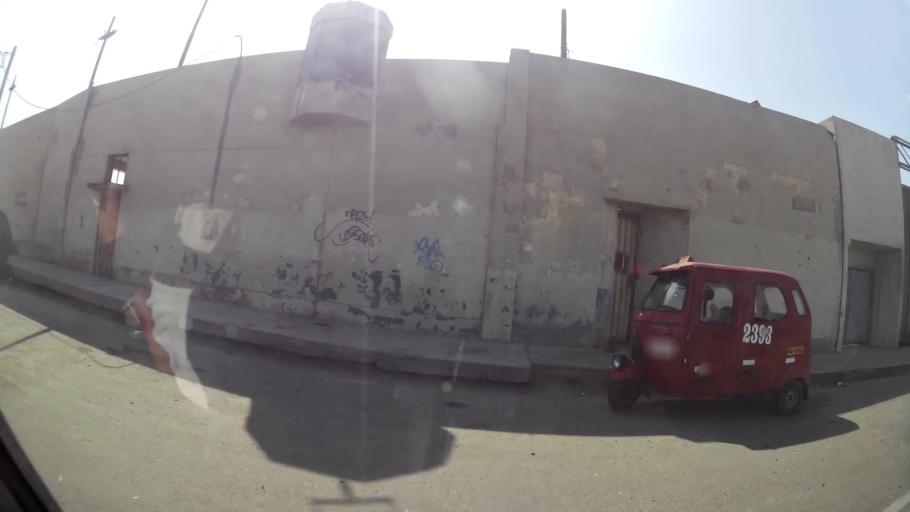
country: PE
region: Lima
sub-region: Huaura
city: Huacho
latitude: -11.1084
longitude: -77.6147
